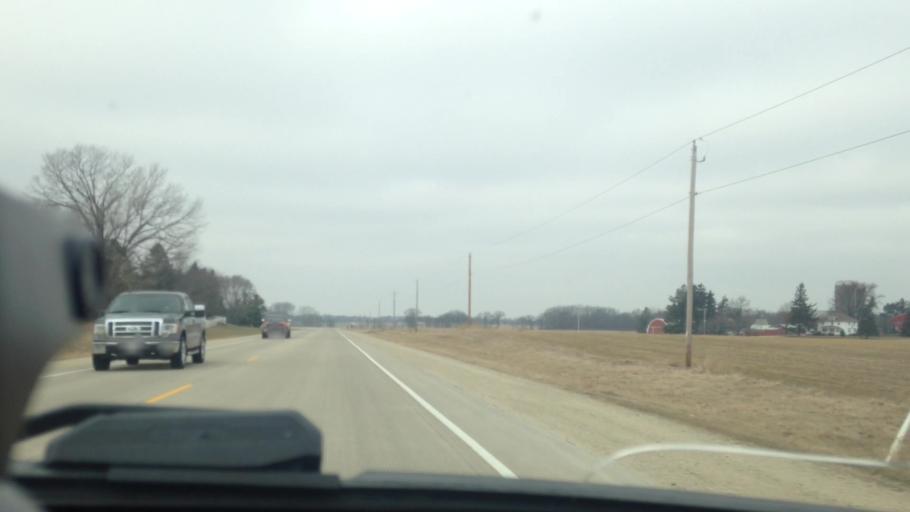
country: US
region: Wisconsin
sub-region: Dodge County
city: Horicon
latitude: 43.4698
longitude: -88.6760
